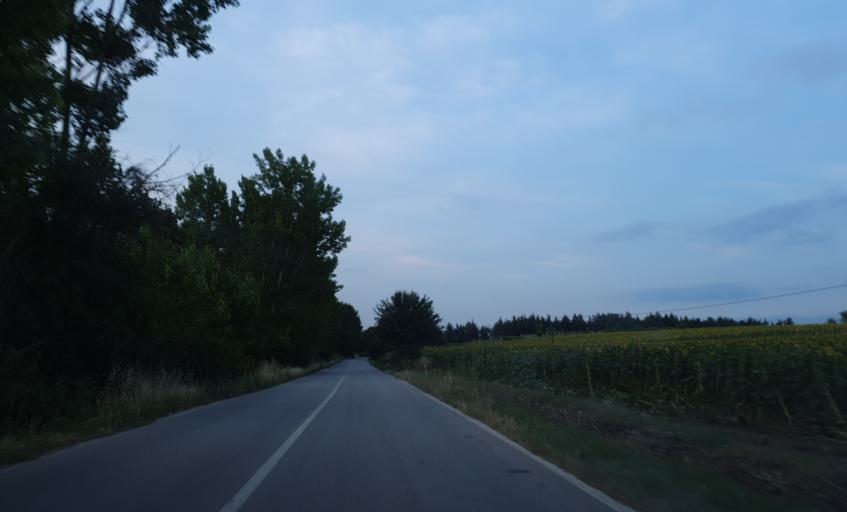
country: TR
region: Tekirdag
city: Beyazkoy
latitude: 41.3735
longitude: 27.6110
